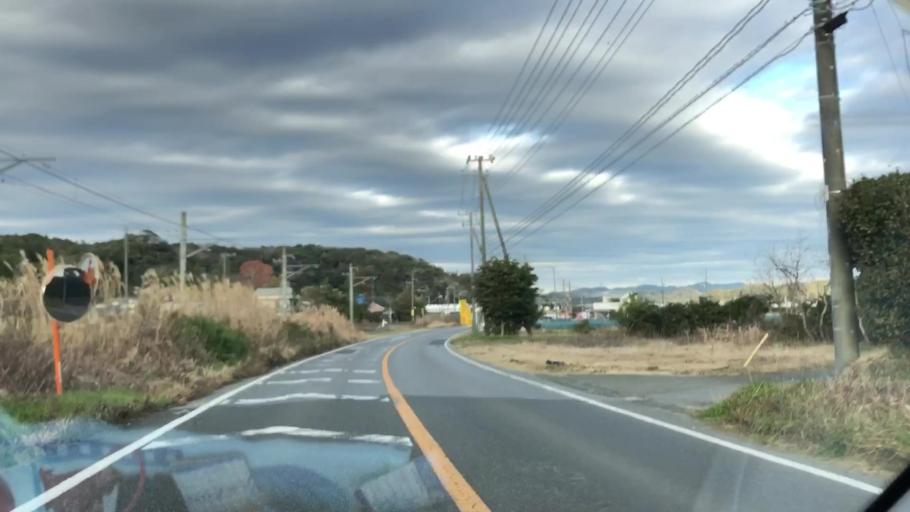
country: JP
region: Chiba
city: Tateyama
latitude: 34.9920
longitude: 139.9216
